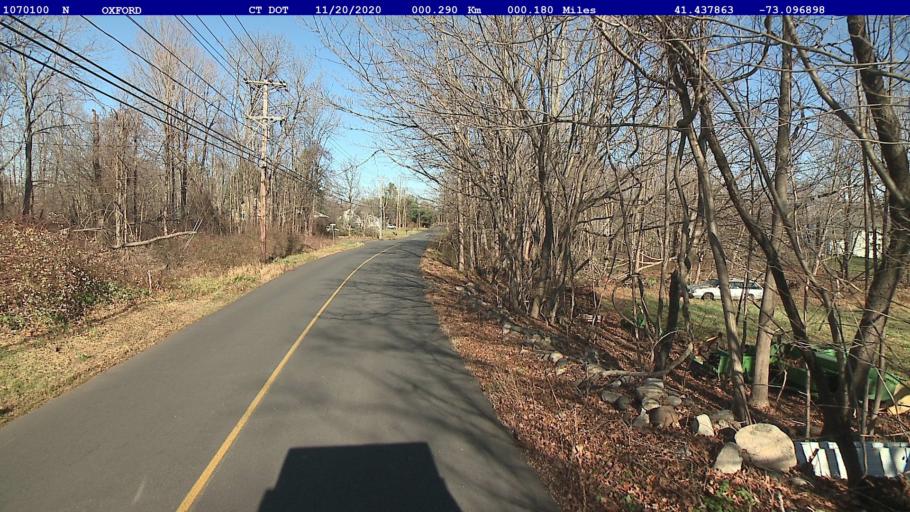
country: US
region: Connecticut
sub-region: New Haven County
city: Oxford
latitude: 41.4379
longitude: -73.0969
